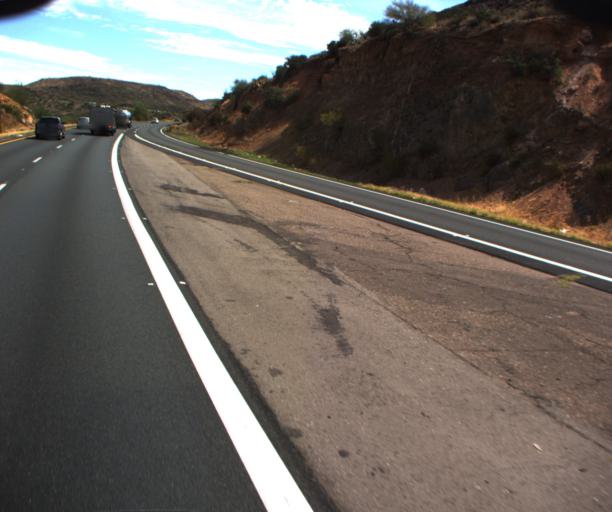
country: US
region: Arizona
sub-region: Yavapai County
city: Black Canyon City
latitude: 34.1381
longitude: -112.1461
